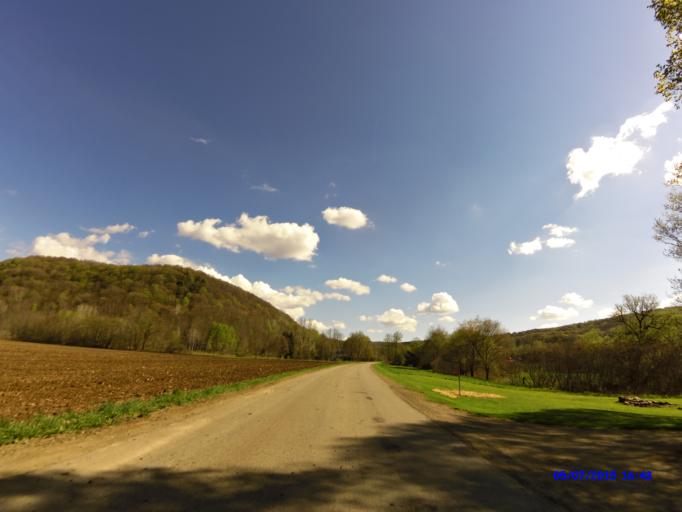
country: US
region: New York
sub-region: Cattaraugus County
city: Little Valley
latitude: 42.3013
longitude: -78.7163
